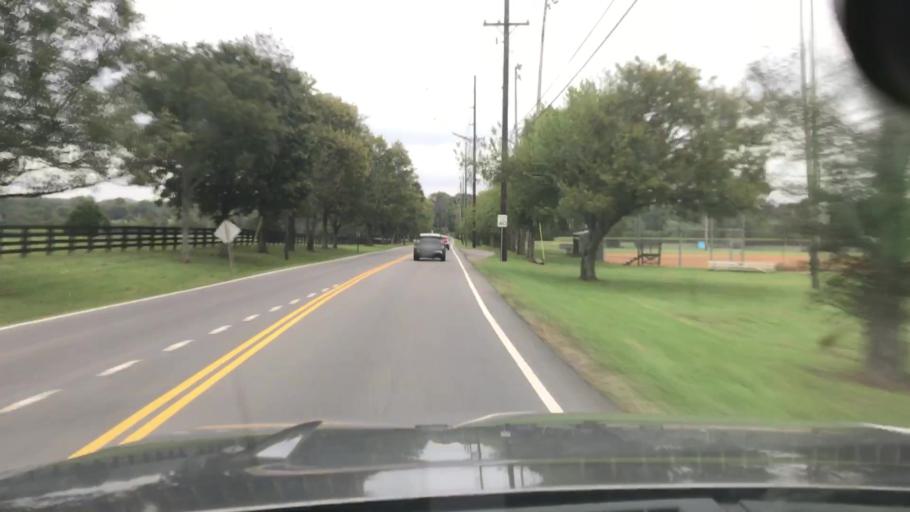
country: US
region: Tennessee
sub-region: Davidson County
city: Forest Hills
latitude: 36.0537
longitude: -86.8980
